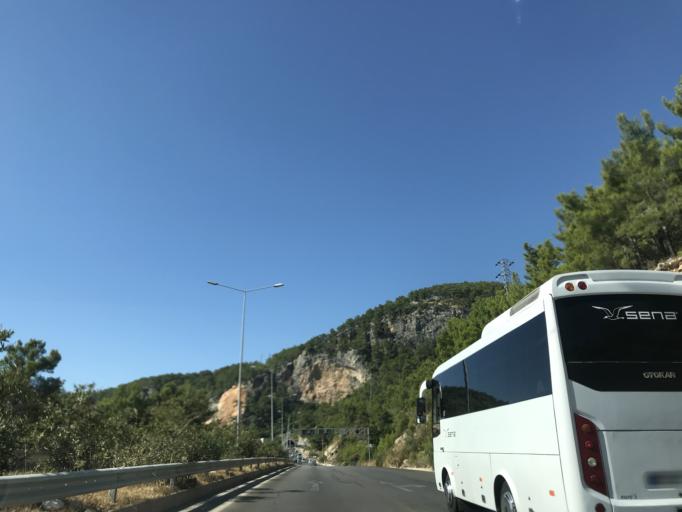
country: TR
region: Antalya
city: Cakirlar
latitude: 36.7557
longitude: 30.5685
